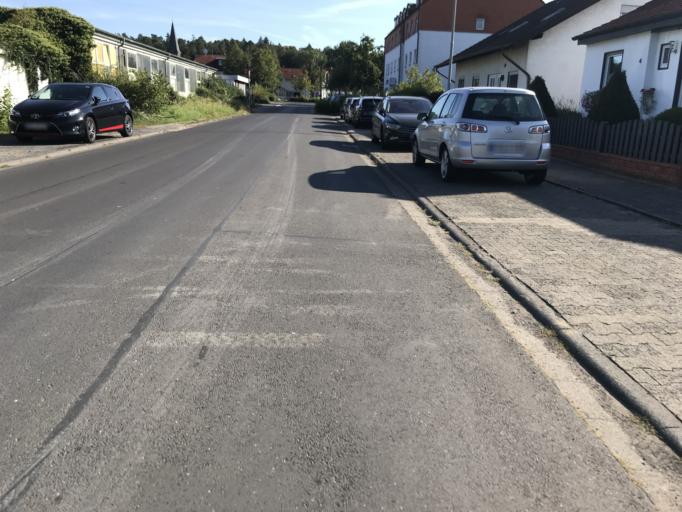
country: DE
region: Hesse
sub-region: Regierungsbezirk Darmstadt
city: Altenstadt
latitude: 50.2702
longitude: 8.9637
